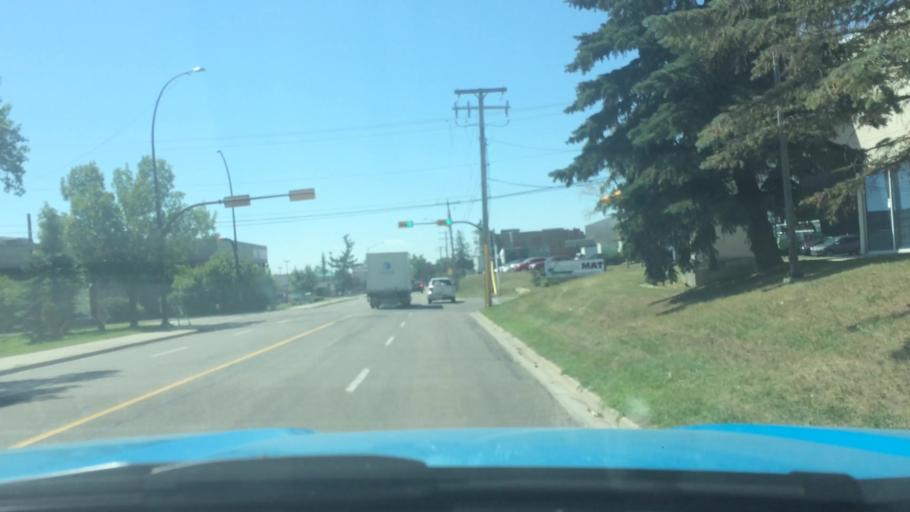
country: CA
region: Alberta
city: Calgary
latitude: 51.0529
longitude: -113.9934
